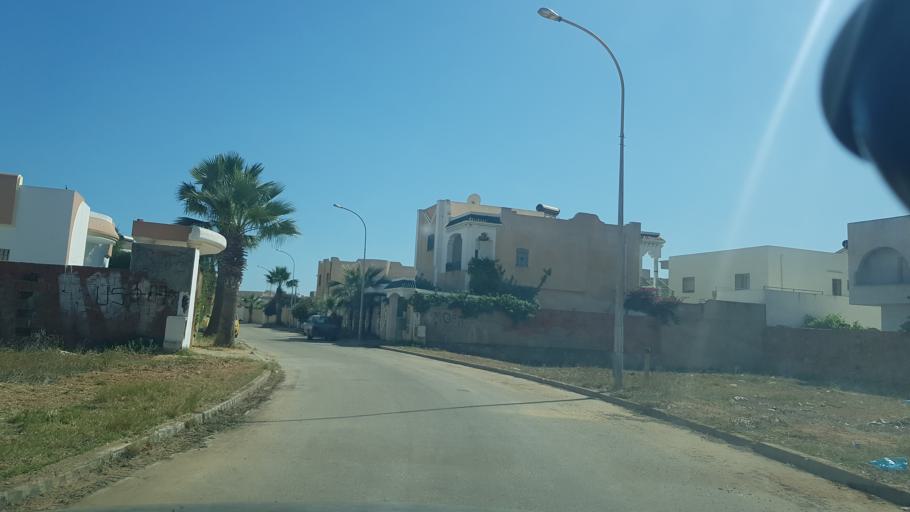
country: TN
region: Safaqis
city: Al Qarmadah
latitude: 34.8291
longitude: 10.7563
